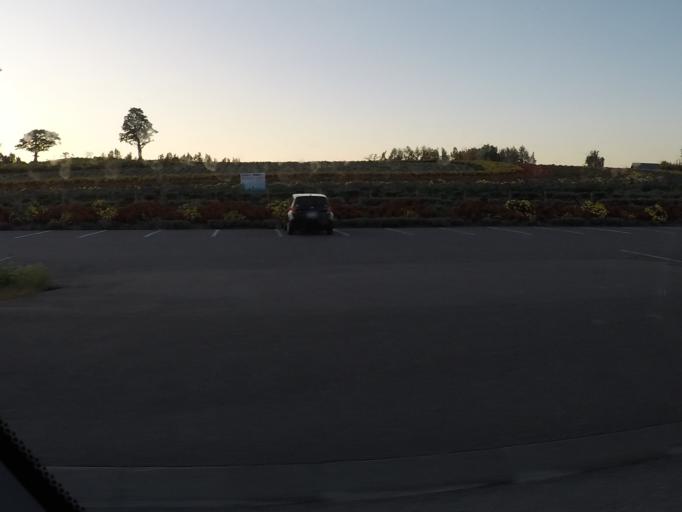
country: JP
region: Hokkaido
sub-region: Asahikawa-shi
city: Asahikawa
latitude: 43.6064
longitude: 142.4705
